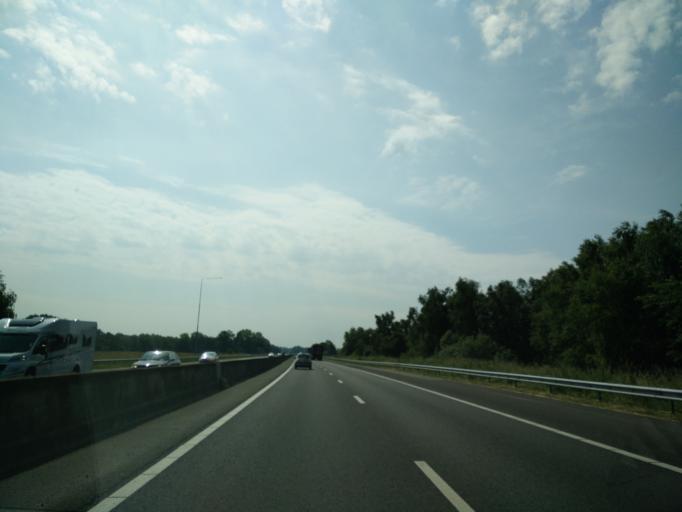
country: NL
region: Groningen
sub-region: Gemeente Haren
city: Haren
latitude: 53.1584
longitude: 6.5959
